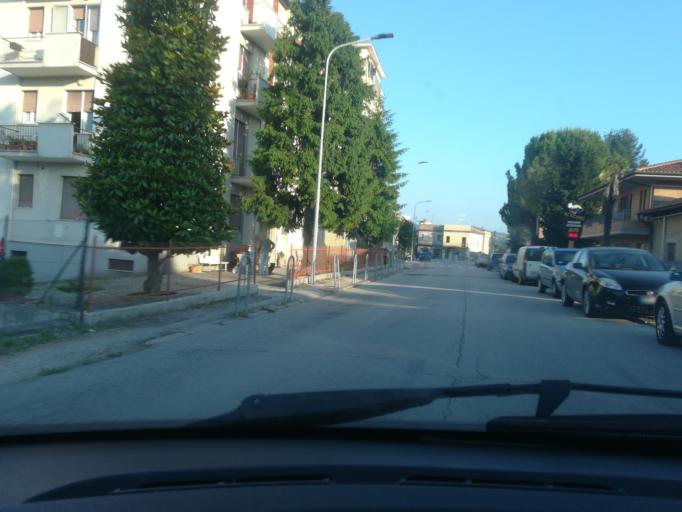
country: IT
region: The Marches
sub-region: Provincia di Macerata
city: Piediripa
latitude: 43.2761
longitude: 13.4841
